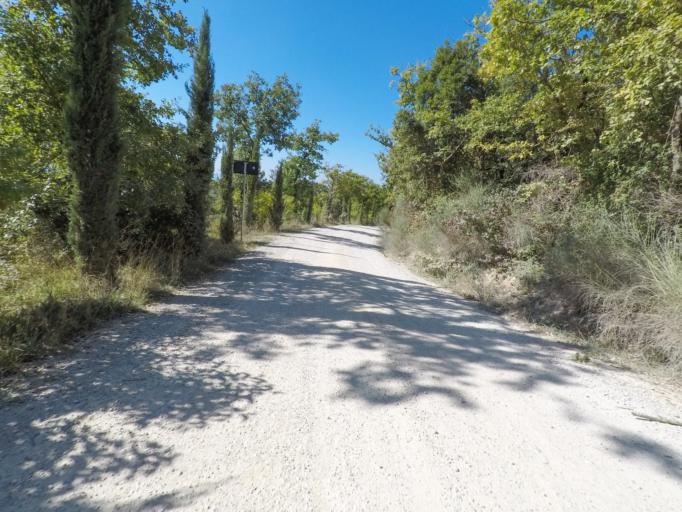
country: IT
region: Tuscany
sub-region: Provincia di Siena
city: Castellina in Chianti
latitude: 43.4365
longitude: 11.3289
